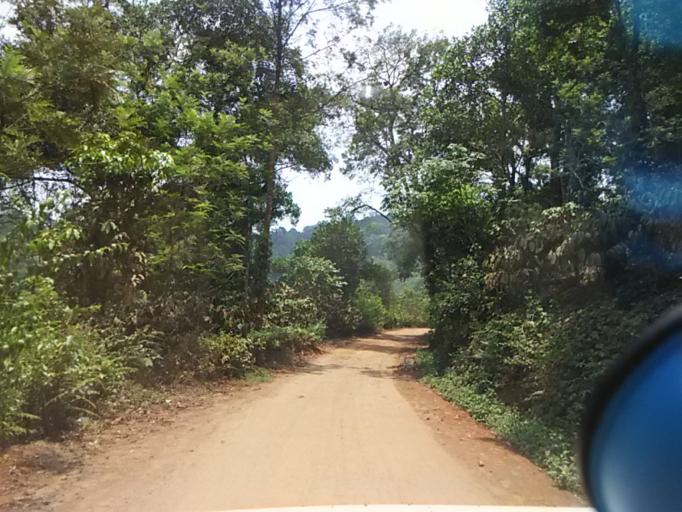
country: IN
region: Karnataka
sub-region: Kodagu
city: Virarajendrapet
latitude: 12.2121
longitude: 75.6760
